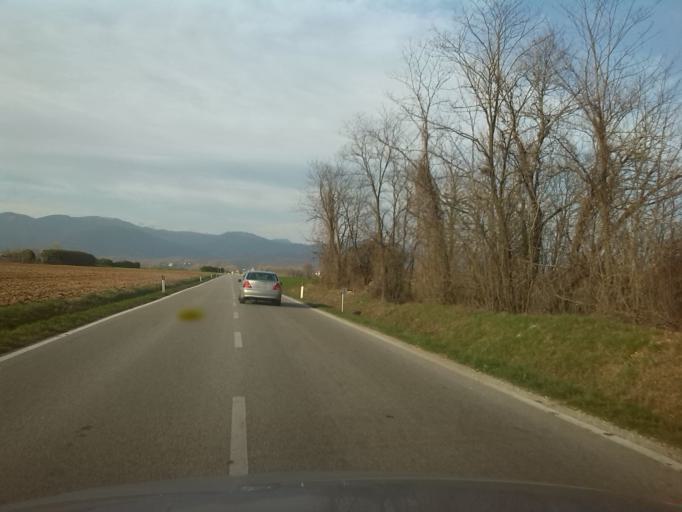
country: IT
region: Friuli Venezia Giulia
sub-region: Provincia di Udine
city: Premariacco
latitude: 46.0631
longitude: 13.4176
